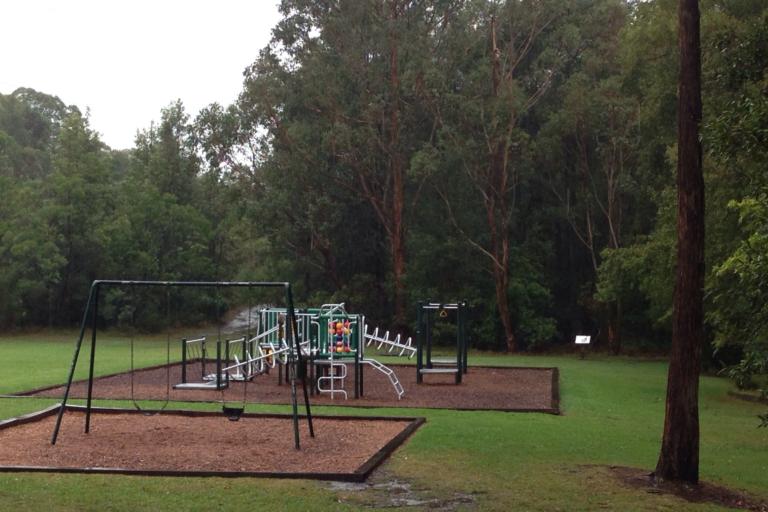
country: AU
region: New South Wales
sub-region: Hornsby Shire
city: Galston
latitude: -33.6377
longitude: 151.0463
